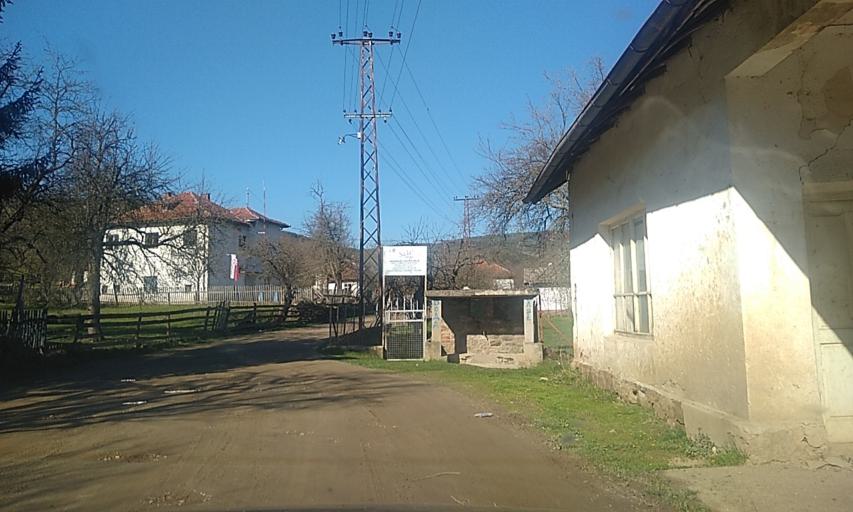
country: RS
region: Central Serbia
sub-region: Pcinjski Okrug
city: Bosilegrad
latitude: 42.3601
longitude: 22.4266
